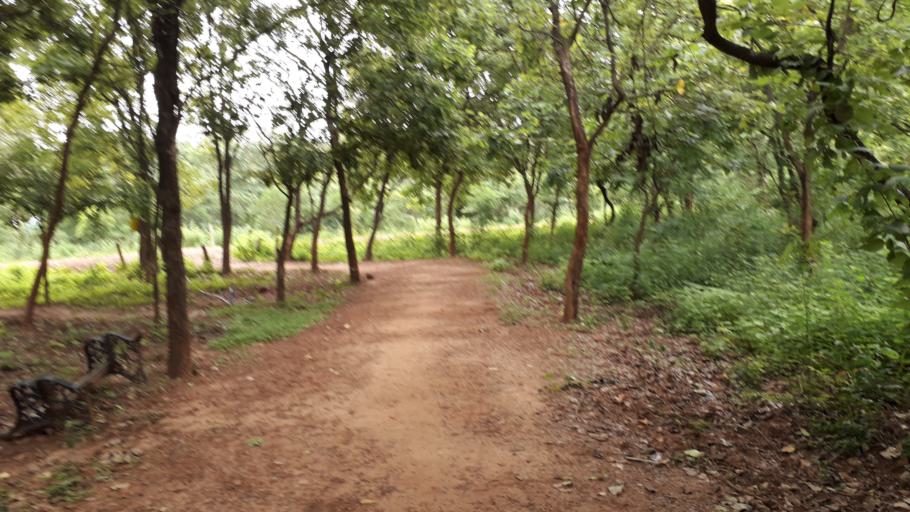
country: IN
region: Andhra Pradesh
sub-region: East Godavari
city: Rajahmundry
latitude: 17.0345
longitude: 81.8216
